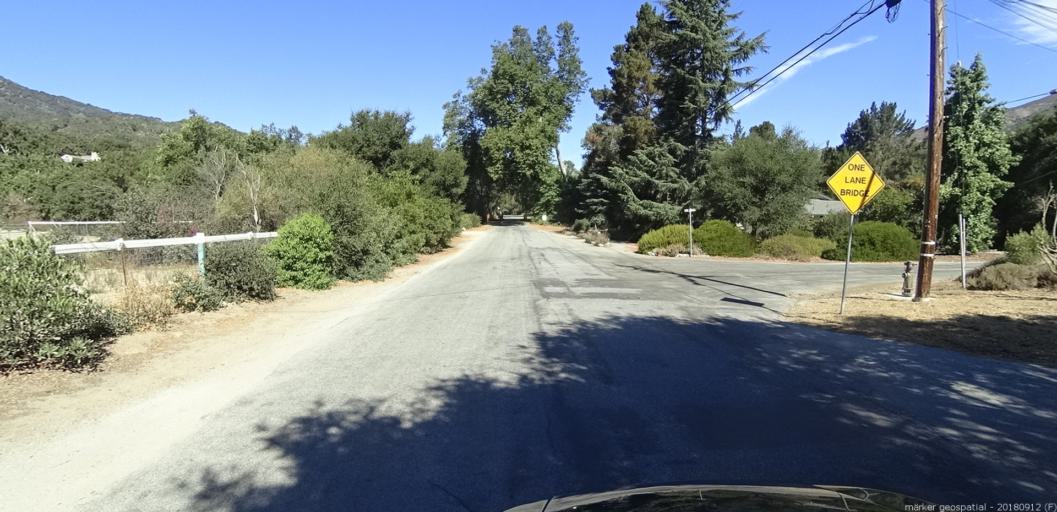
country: US
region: California
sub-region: Monterey County
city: Carmel Valley Village
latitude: 36.4905
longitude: -121.7509
